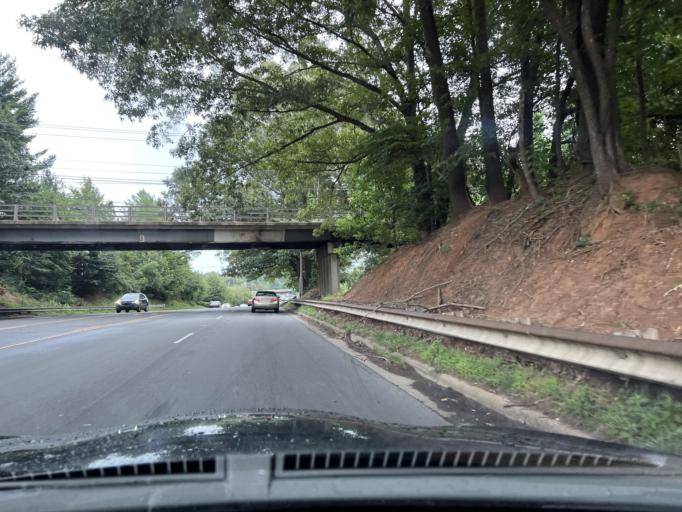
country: US
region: North Carolina
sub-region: Buncombe County
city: Bent Creek
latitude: 35.5557
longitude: -82.6411
